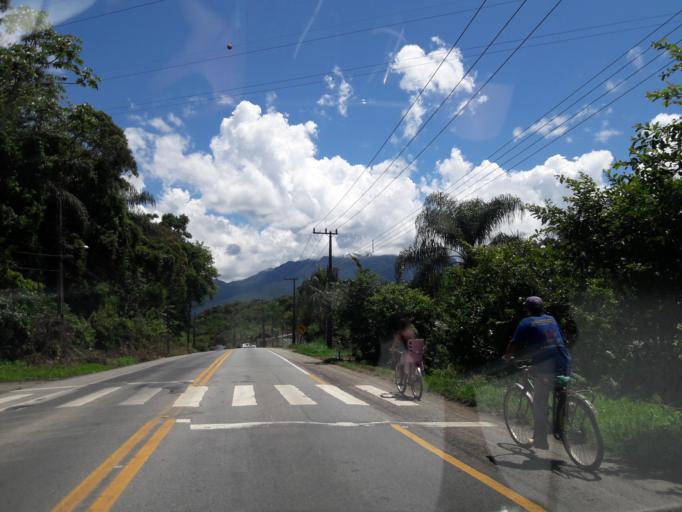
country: BR
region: Parana
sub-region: Antonina
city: Antonina
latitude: -25.4618
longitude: -48.8198
